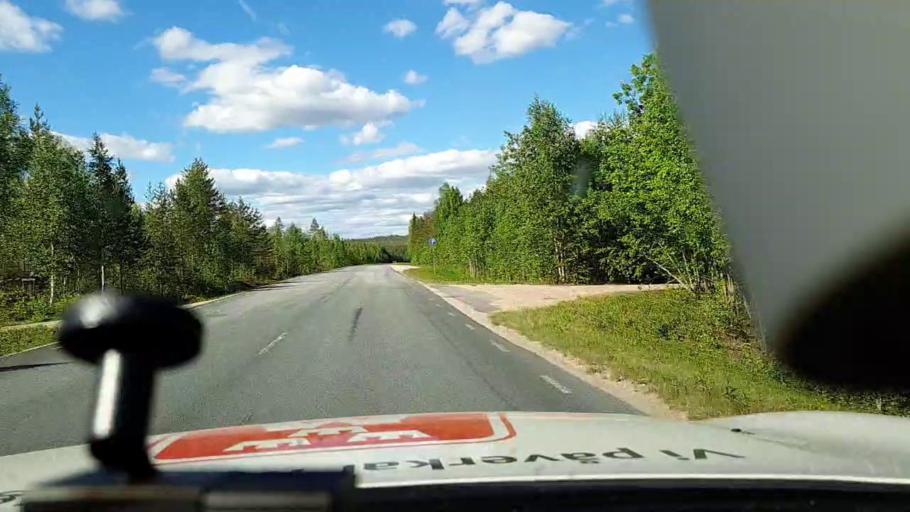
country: FI
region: Lapland
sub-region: Torniolaakso
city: Ylitornio
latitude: 66.3164
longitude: 23.6196
